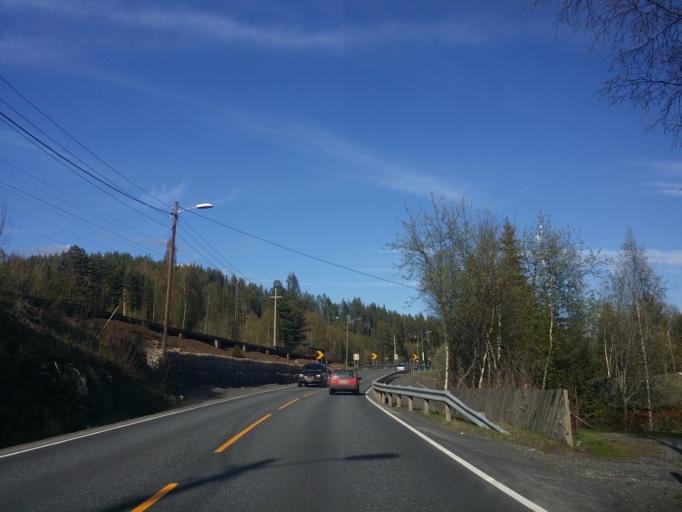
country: NO
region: Buskerud
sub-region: Kongsberg
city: Kongsberg
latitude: 59.6298
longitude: 9.4955
